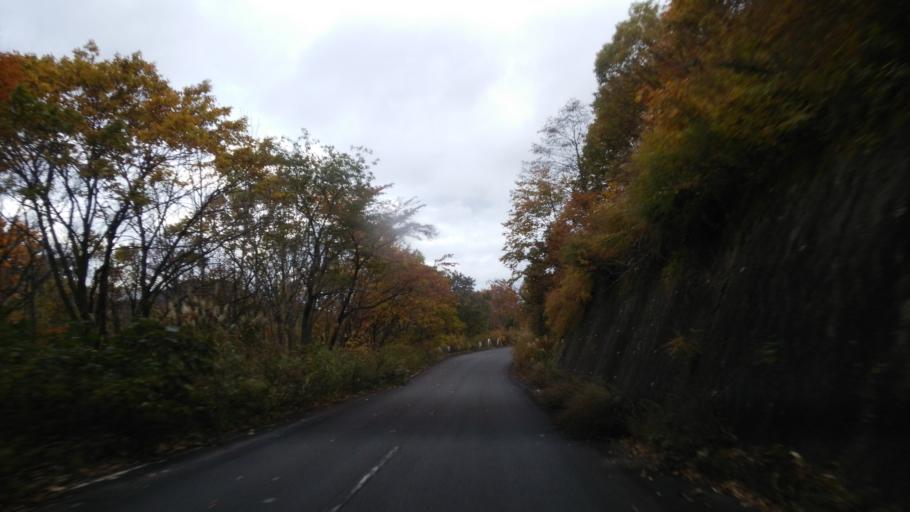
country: JP
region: Fukushima
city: Kitakata
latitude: 37.3955
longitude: 139.7399
